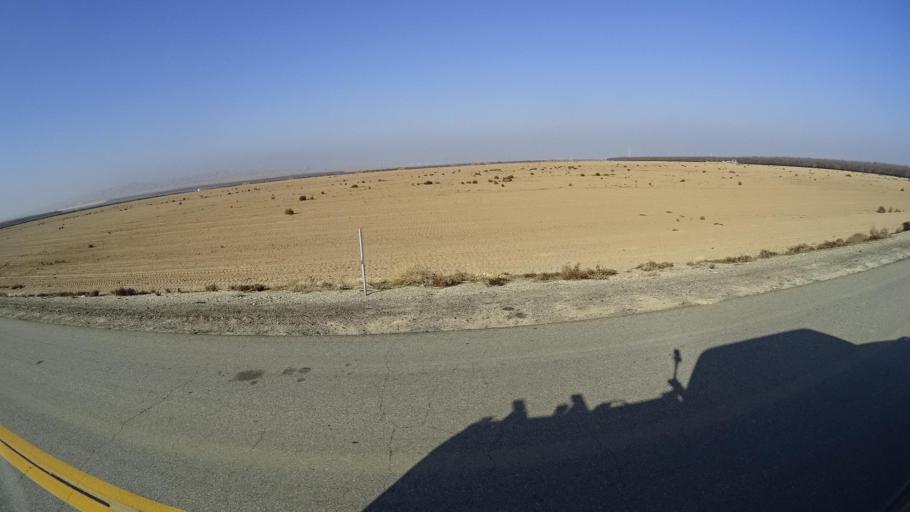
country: US
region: California
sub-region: Kern County
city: Maricopa
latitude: 35.1013
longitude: -119.3352
